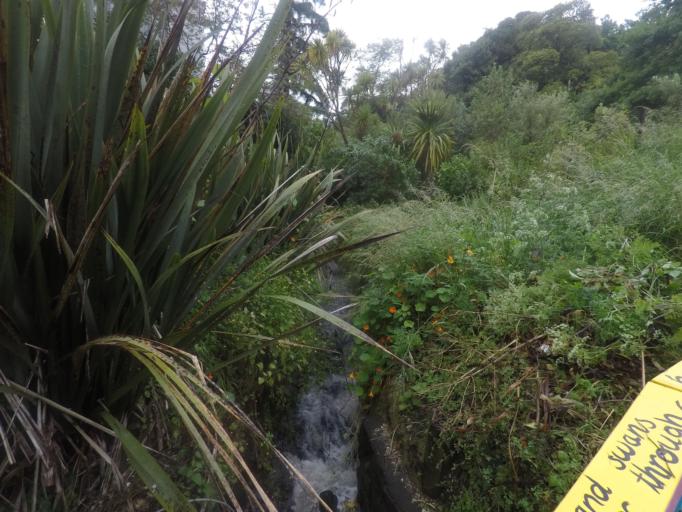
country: NZ
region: Auckland
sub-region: Auckland
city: Auckland
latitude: -36.8563
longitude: 174.7787
